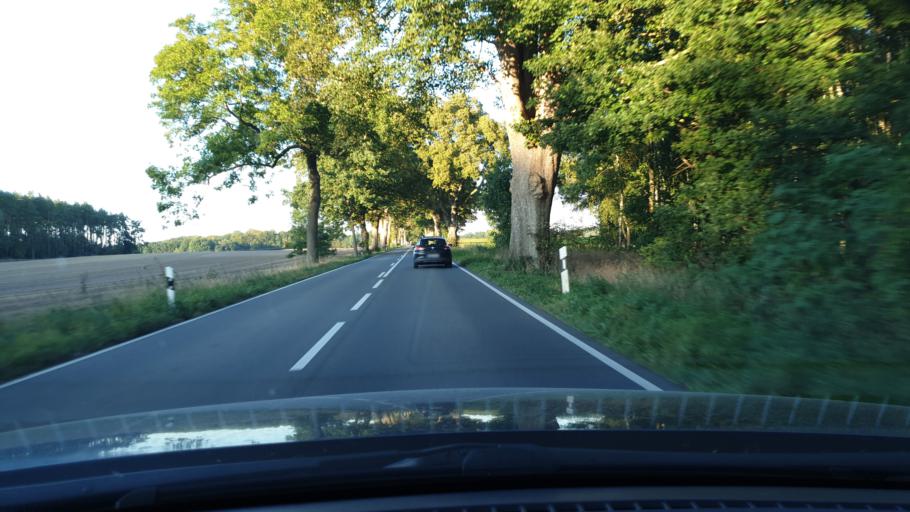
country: DE
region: Mecklenburg-Vorpommern
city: Lutzow
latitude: 53.5918
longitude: 11.1215
